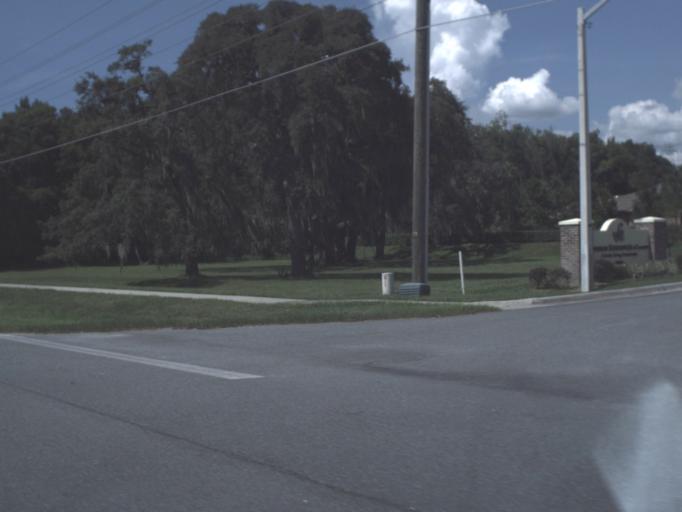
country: US
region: Florida
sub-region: Citrus County
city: Lecanto
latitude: 28.8703
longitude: -82.5144
